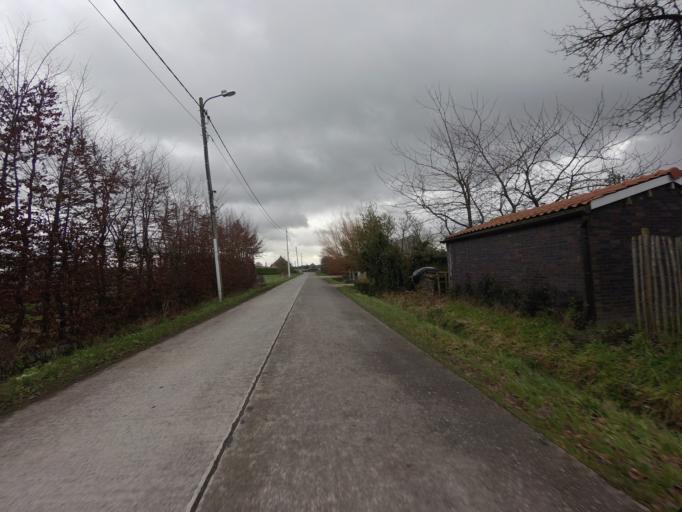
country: BE
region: Flanders
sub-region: Provincie Antwerpen
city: Duffel
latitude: 51.0809
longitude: 4.5166
